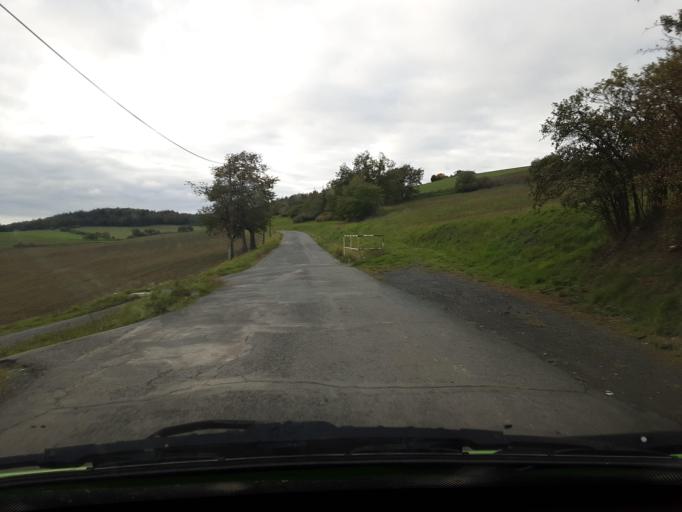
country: CZ
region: Plzensky
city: Janovice nad Uhlavou
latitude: 49.4272
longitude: 13.1744
